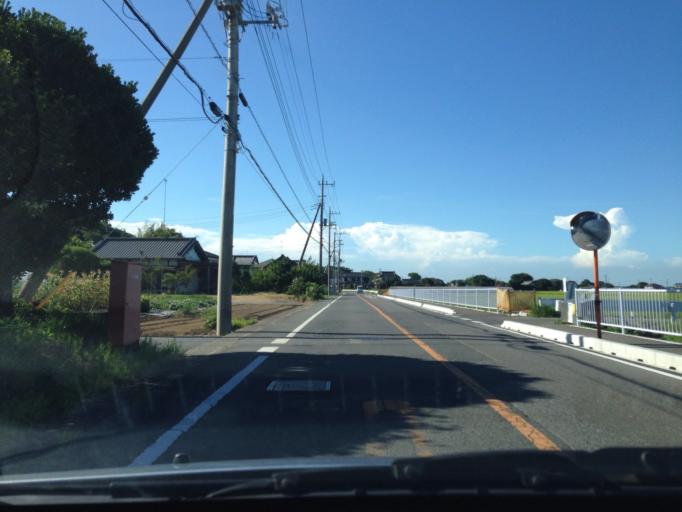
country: JP
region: Ibaraki
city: Inashiki
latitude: 36.0069
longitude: 140.3660
